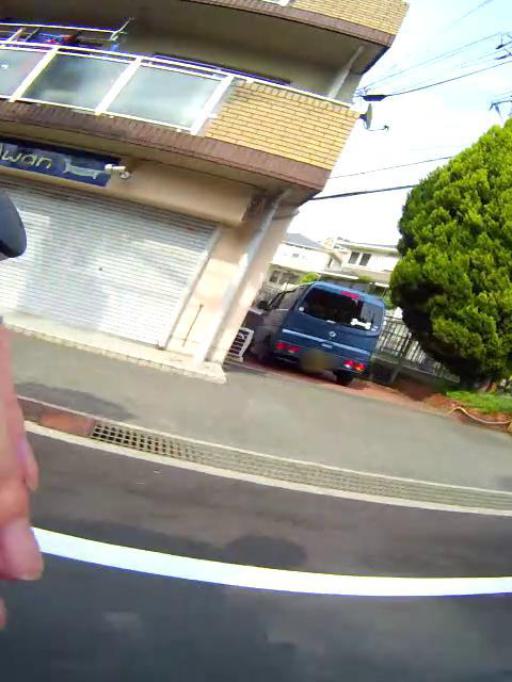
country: JP
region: Osaka
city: Toyonaka
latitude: 34.7807
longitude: 135.4874
